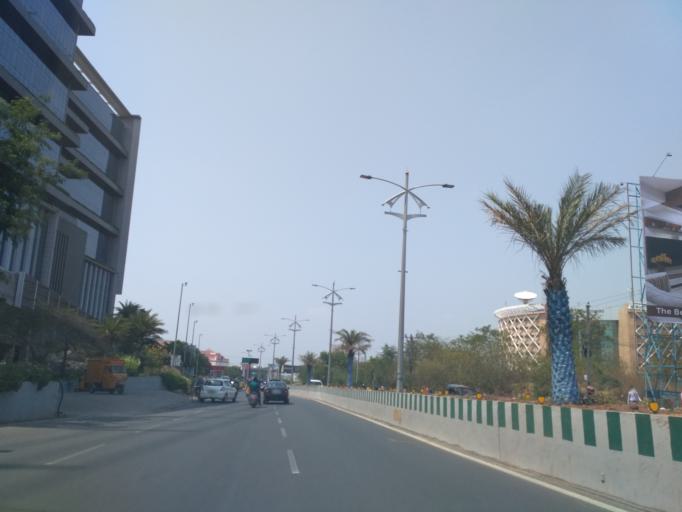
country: IN
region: Telangana
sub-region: Rangareddi
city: Kukatpalli
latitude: 17.4486
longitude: 78.3790
